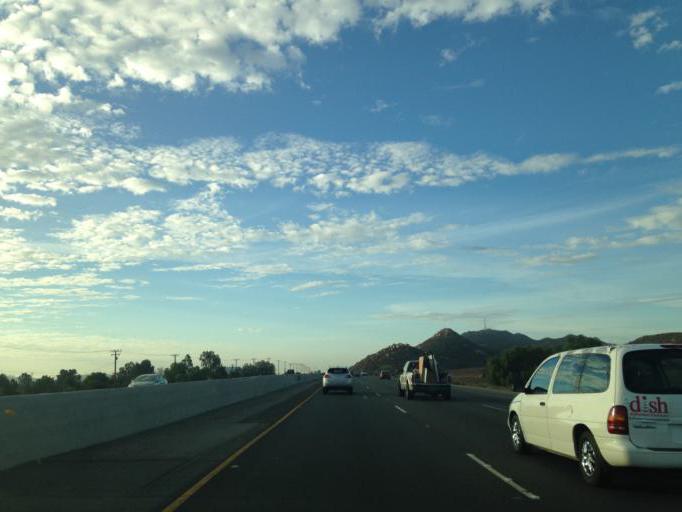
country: US
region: California
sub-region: Riverside County
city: Murrieta Hot Springs
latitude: 33.6264
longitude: -117.1711
